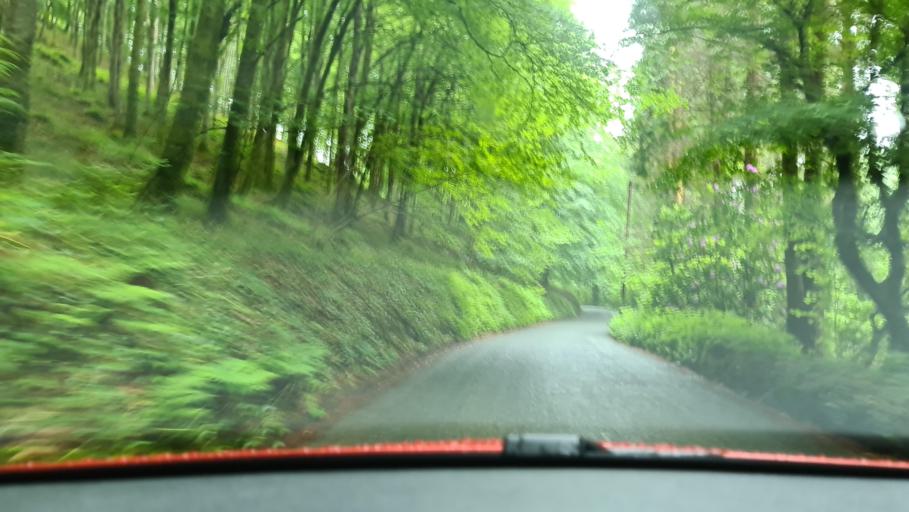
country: GB
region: England
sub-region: Cornwall
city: Liskeard
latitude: 50.4590
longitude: -4.5565
